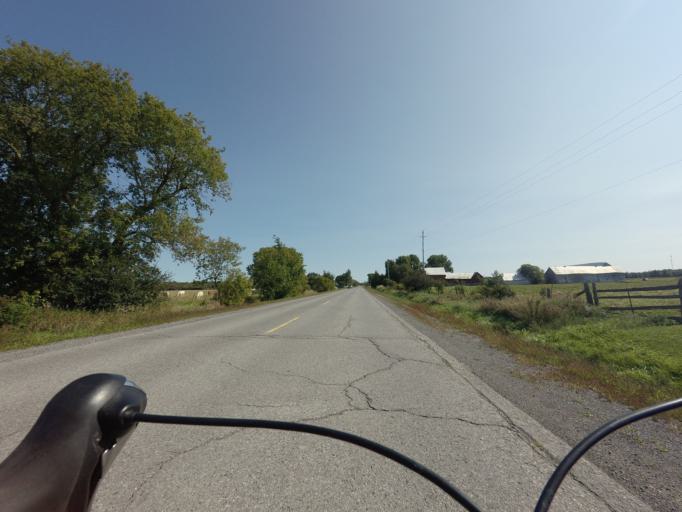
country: CA
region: Ontario
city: Carleton Place
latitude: 45.3406
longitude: -76.1007
